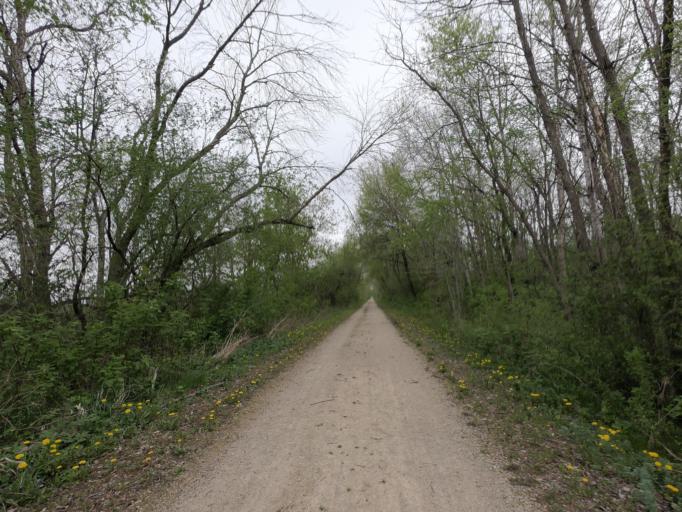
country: US
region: Wisconsin
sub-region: Jefferson County
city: Johnson Creek
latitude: 43.0282
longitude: -88.7399
